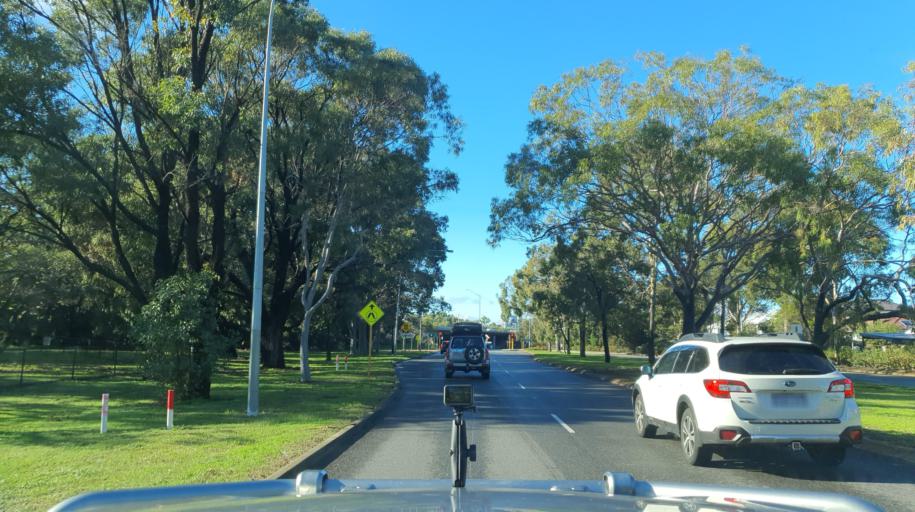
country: AU
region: Western Australia
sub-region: Vincent
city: Leederville
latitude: -31.9346
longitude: 115.8357
